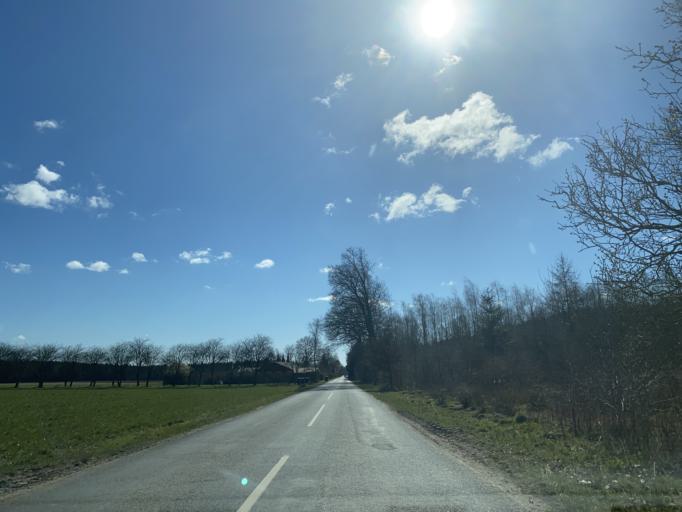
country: DK
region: Central Jutland
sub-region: Silkeborg Kommune
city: Svejbaek
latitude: 56.2439
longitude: 9.6598
